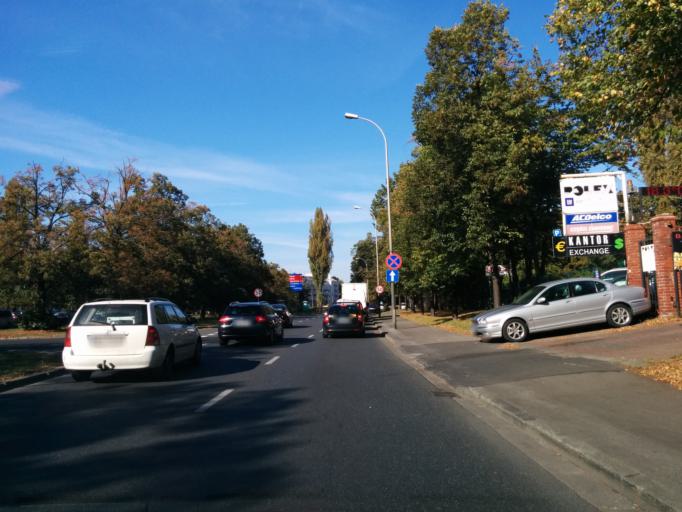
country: PL
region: Masovian Voivodeship
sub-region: Warszawa
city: Ochota
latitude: 52.2139
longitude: 20.9888
